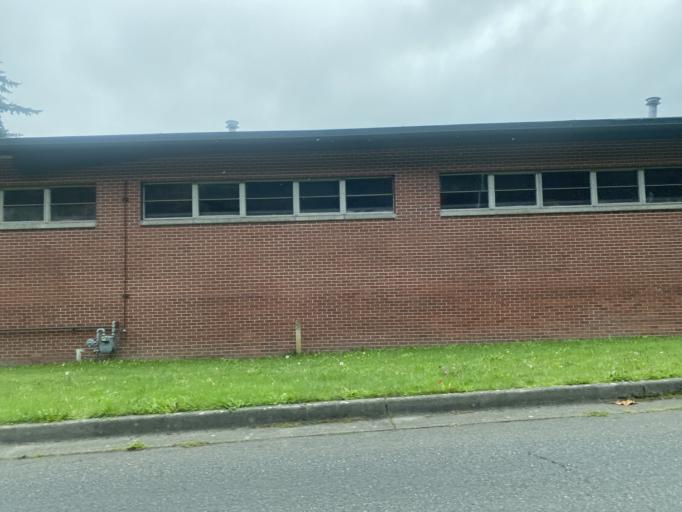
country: US
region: Washington
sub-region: King County
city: Seattle
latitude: 47.6614
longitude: -122.4056
